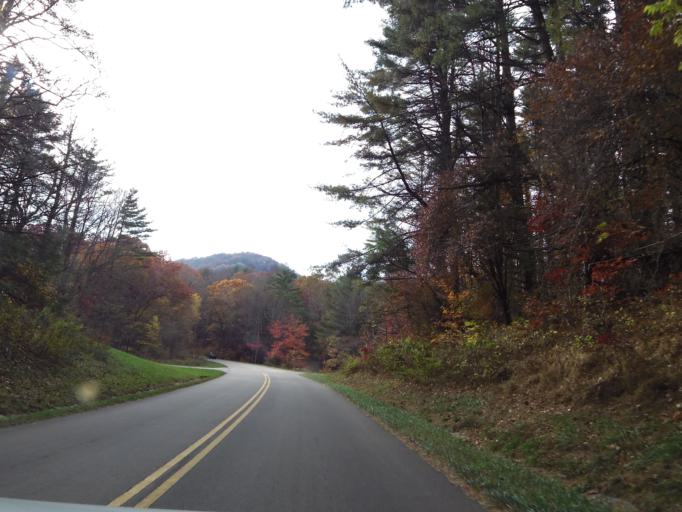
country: US
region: North Carolina
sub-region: Wilkes County
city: Mulberry
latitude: 36.3907
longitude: -81.2659
